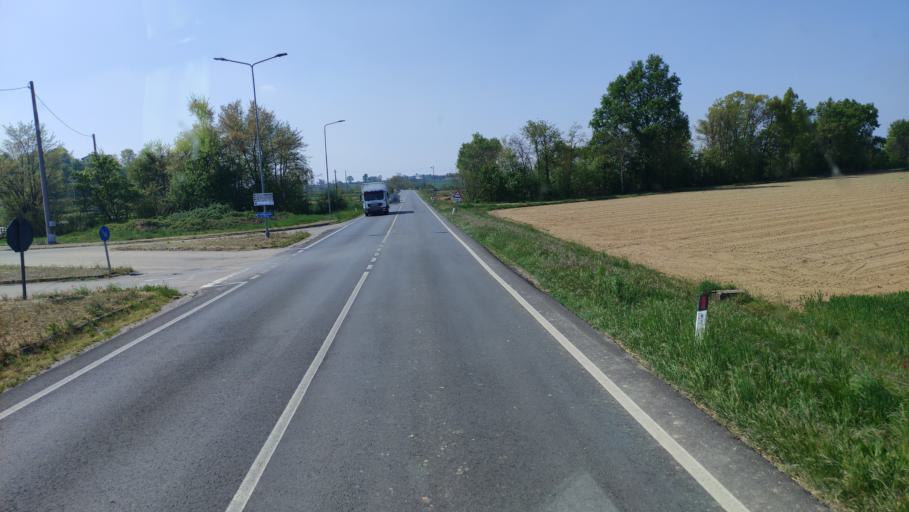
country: IT
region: Piedmont
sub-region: Provincia di Cuneo
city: Marene
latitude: 44.6654
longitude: 7.7689
